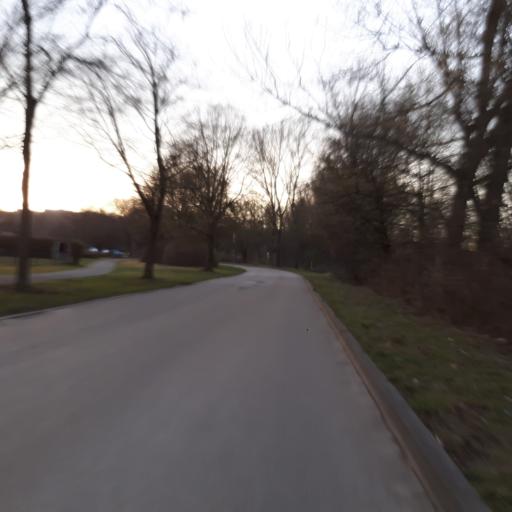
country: DE
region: Baden-Wuerttemberg
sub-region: Regierungsbezirk Stuttgart
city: Freiberg am Neckar
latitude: 48.9431
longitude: 9.1925
